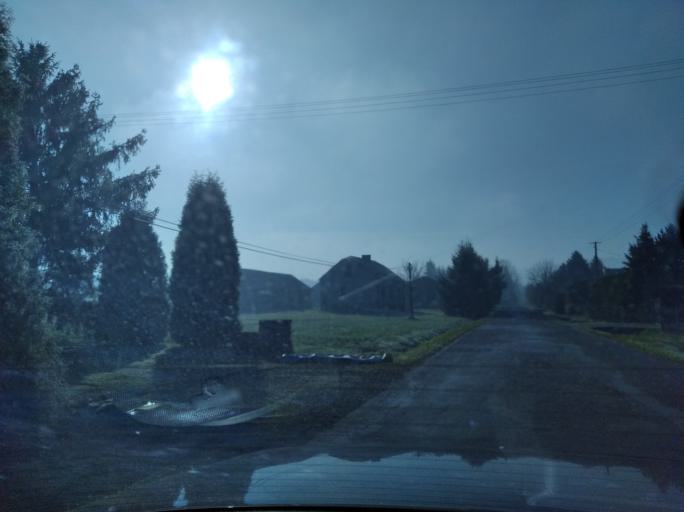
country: PL
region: Subcarpathian Voivodeship
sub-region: Powiat strzyzowski
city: Wysoka Strzyzowska
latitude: 49.8577
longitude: 21.7055
